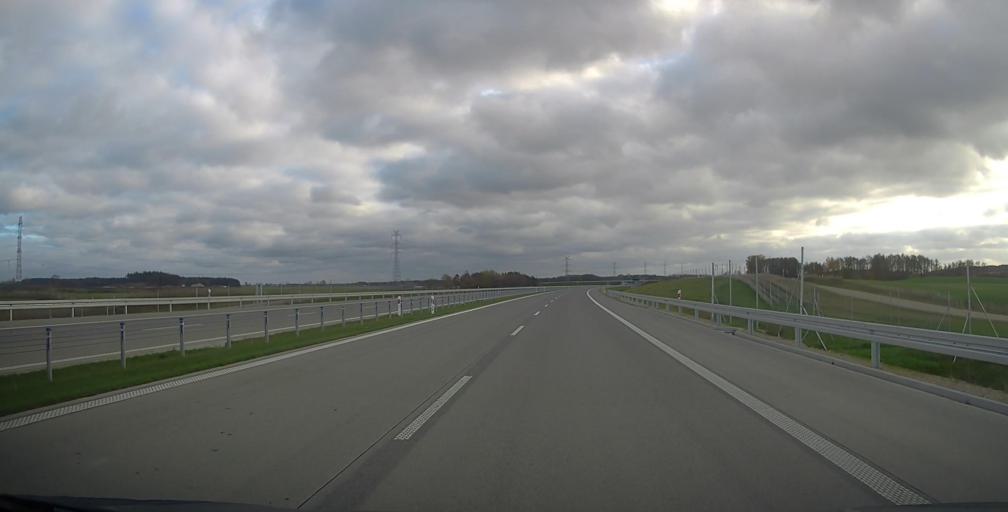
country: PL
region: Podlasie
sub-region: Powiat grajewski
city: Szczuczyn
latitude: 53.6111
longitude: 22.3193
